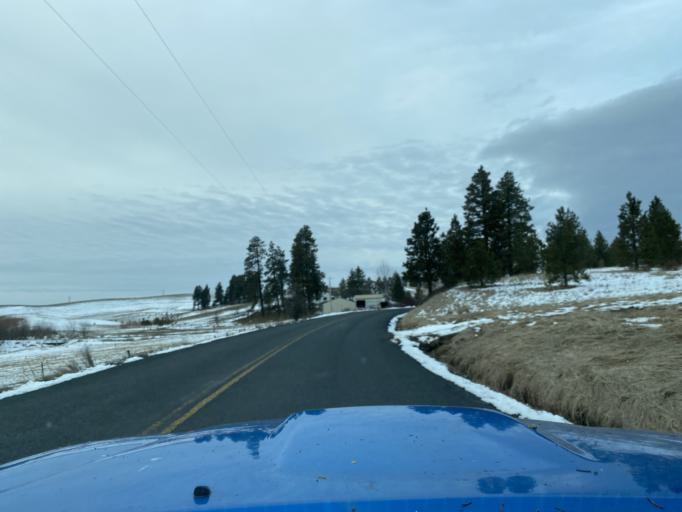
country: US
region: Idaho
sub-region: Latah County
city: Moscow
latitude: 46.6960
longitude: -116.9265
